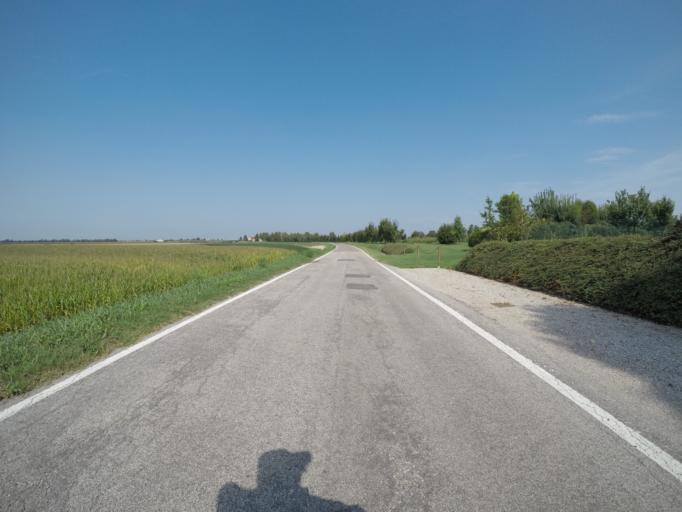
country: IT
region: Veneto
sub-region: Provincia di Rovigo
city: Villanova del Ghebbo Canton
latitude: 45.0625
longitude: 11.6241
